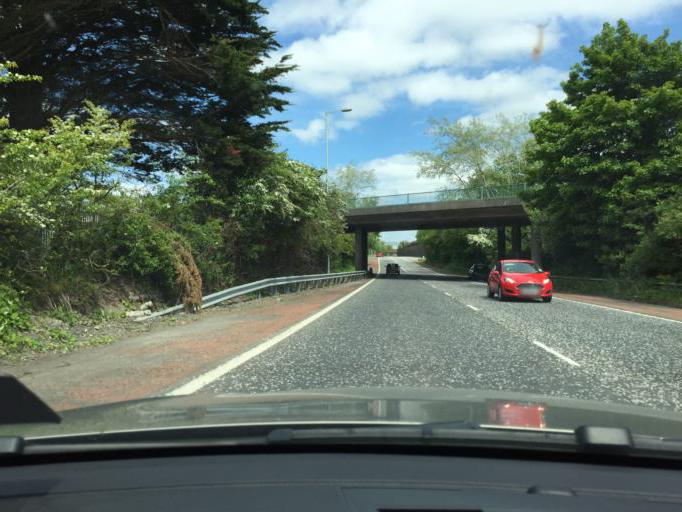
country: GB
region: Northern Ireland
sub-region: Armagh District
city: Portadown
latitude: 54.4191
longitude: -6.4574
